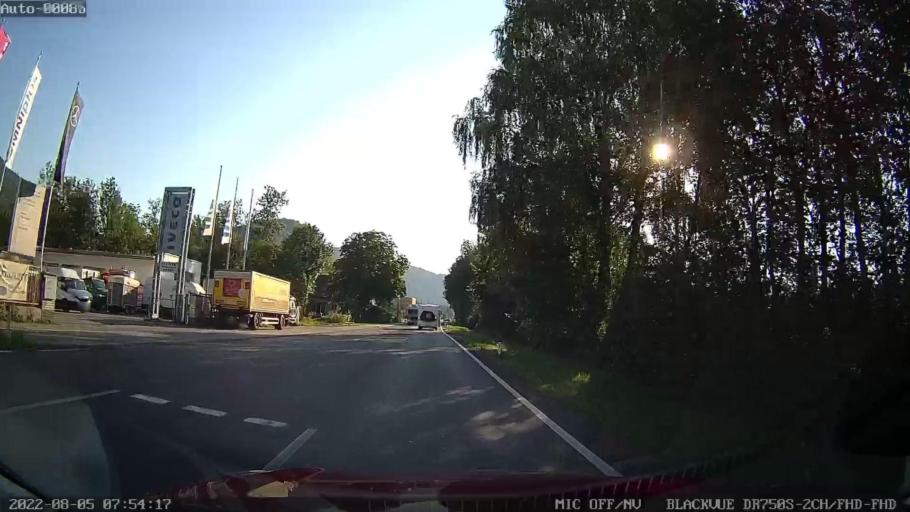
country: AT
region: Carinthia
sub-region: Politischer Bezirk Villach Land
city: Finkenstein am Faaker See
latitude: 46.5669
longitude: 13.8054
